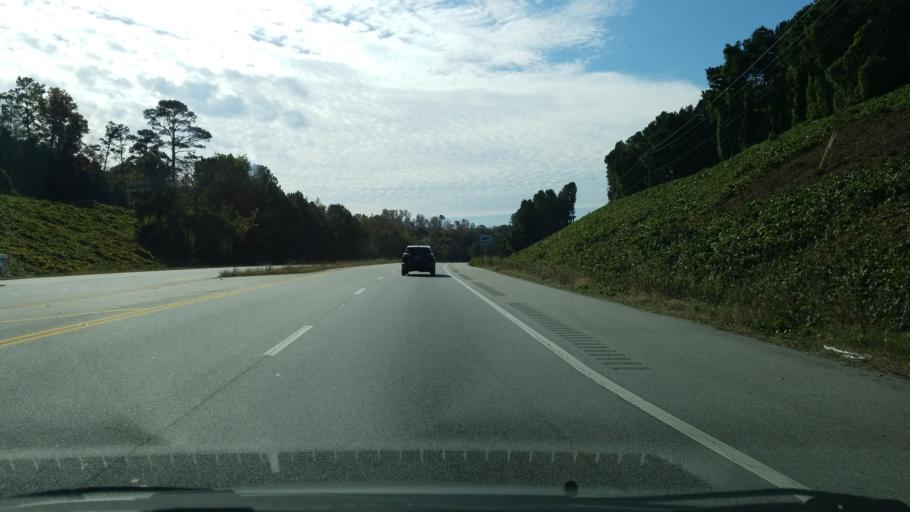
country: US
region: Tennessee
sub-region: Hamilton County
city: Harrison
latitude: 35.1342
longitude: -85.1220
